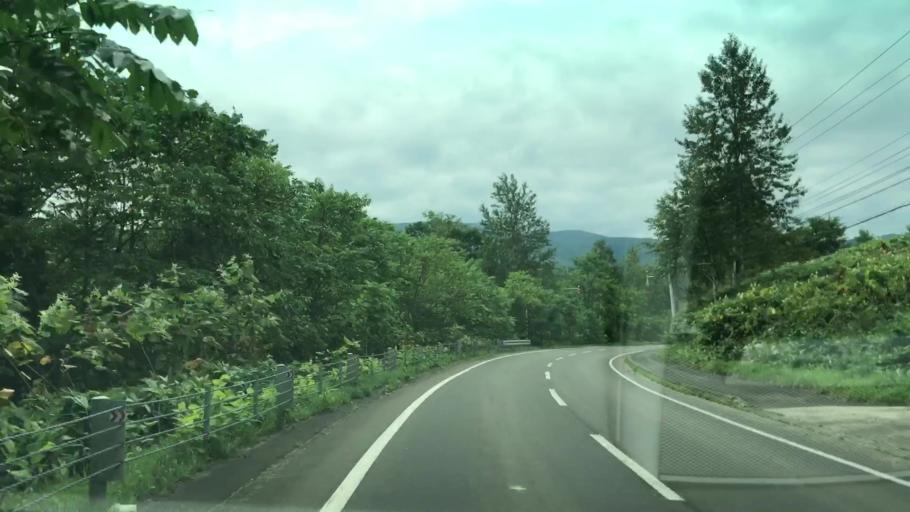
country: JP
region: Hokkaido
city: Yoichi
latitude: 43.0655
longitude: 140.8208
